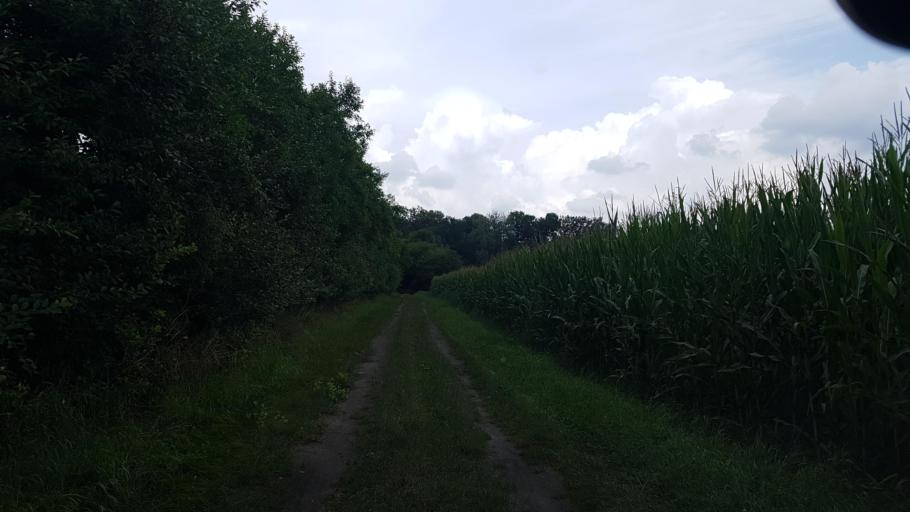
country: DE
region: Brandenburg
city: Sonnewalde
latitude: 51.6950
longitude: 13.6303
